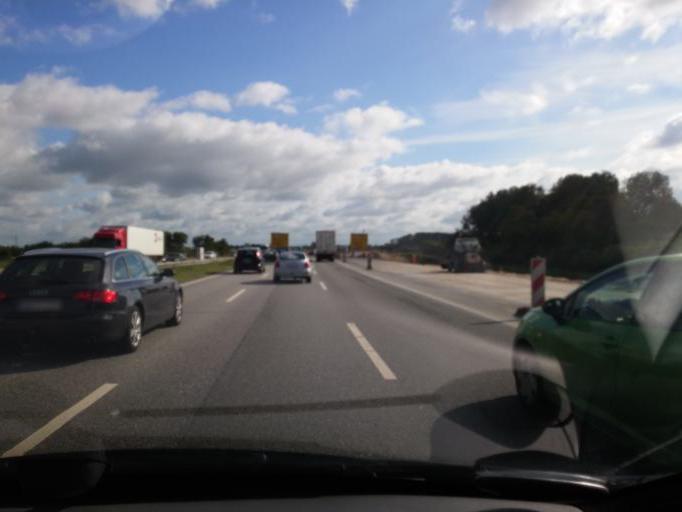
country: DK
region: Zealand
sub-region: Solrod Kommune
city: Solrod
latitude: 55.5123
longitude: 12.1819
